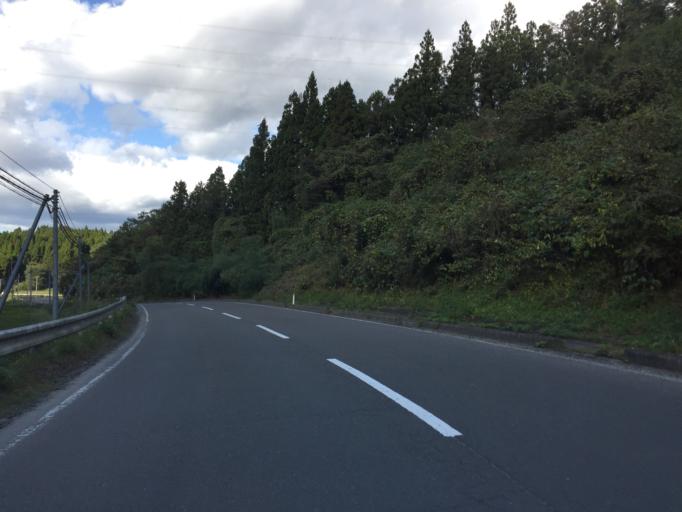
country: JP
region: Miyagi
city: Marumori
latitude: 37.8563
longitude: 140.8302
